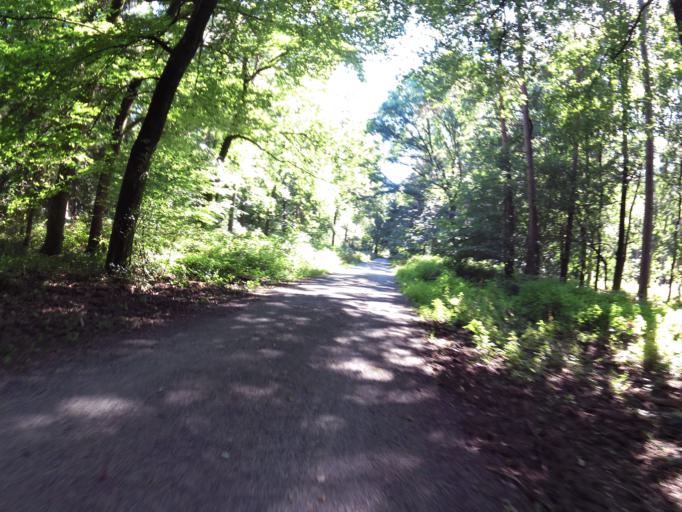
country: NL
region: Gelderland
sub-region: Gemeente Groesbeek
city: De Horst
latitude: 51.7432
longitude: 5.9840
